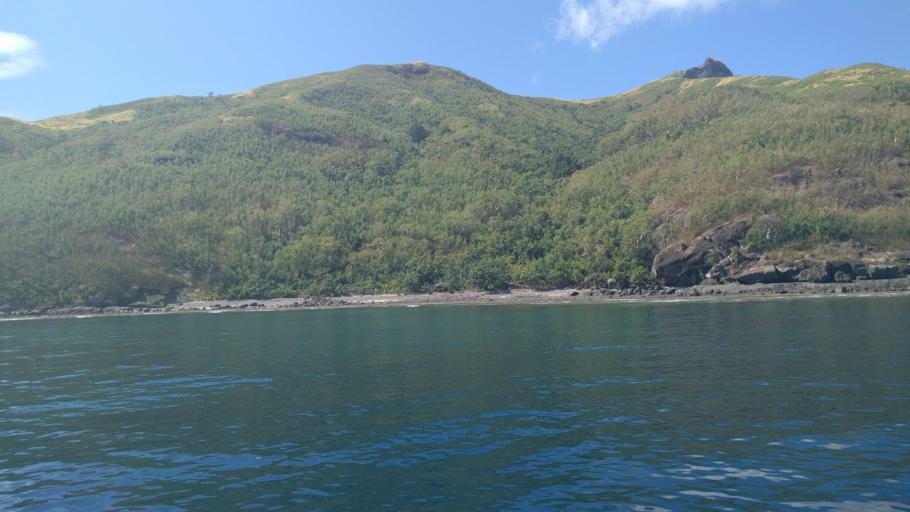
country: FJ
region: Western
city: Lautoka
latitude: -17.2842
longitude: 177.1028
